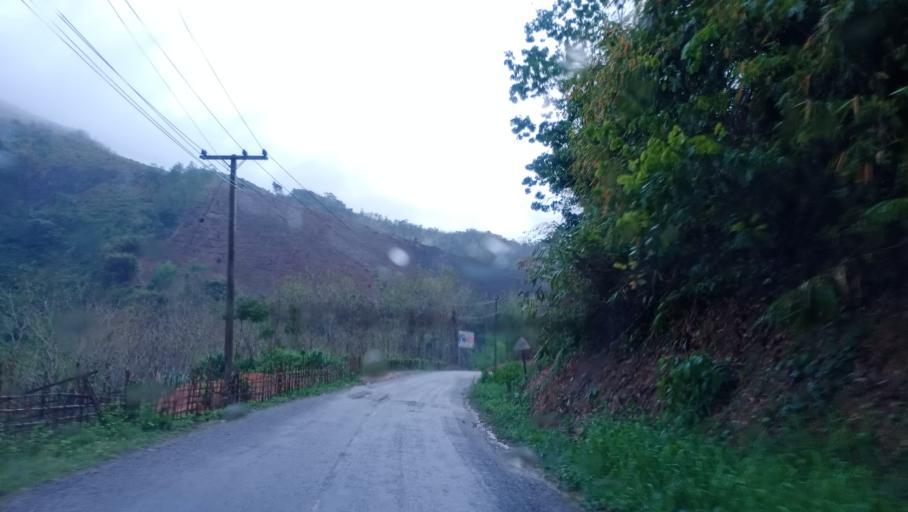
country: LA
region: Phongsali
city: Khoa
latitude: 21.0635
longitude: 102.4847
